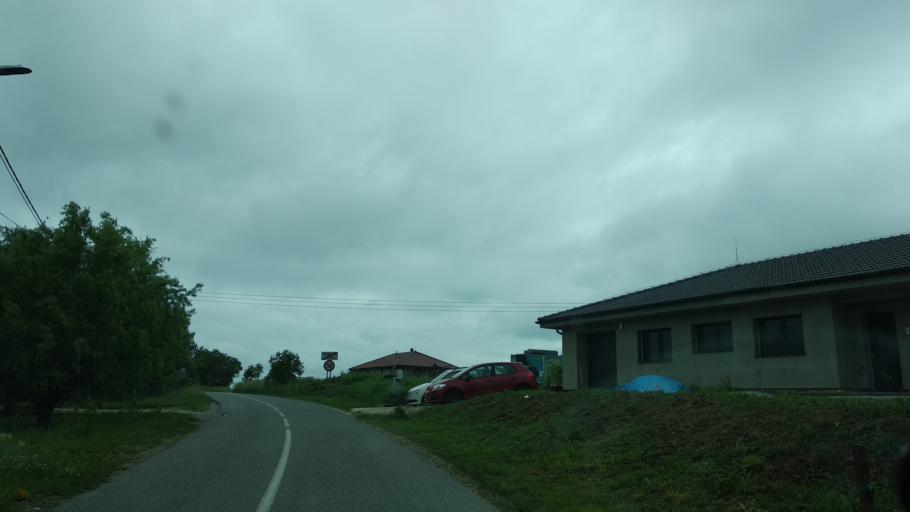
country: SK
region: Trenciansky
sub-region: Okres Trencin
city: Trencin
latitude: 48.7973
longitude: 18.1168
